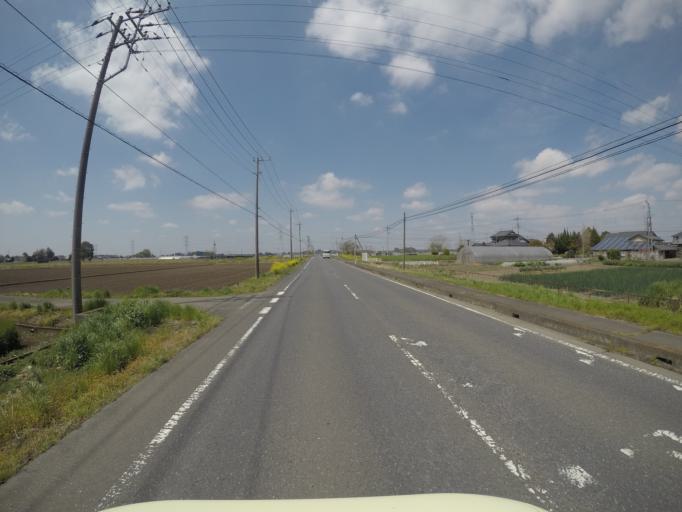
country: JP
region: Ibaraki
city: Shimodate
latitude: 36.3382
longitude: 139.9616
